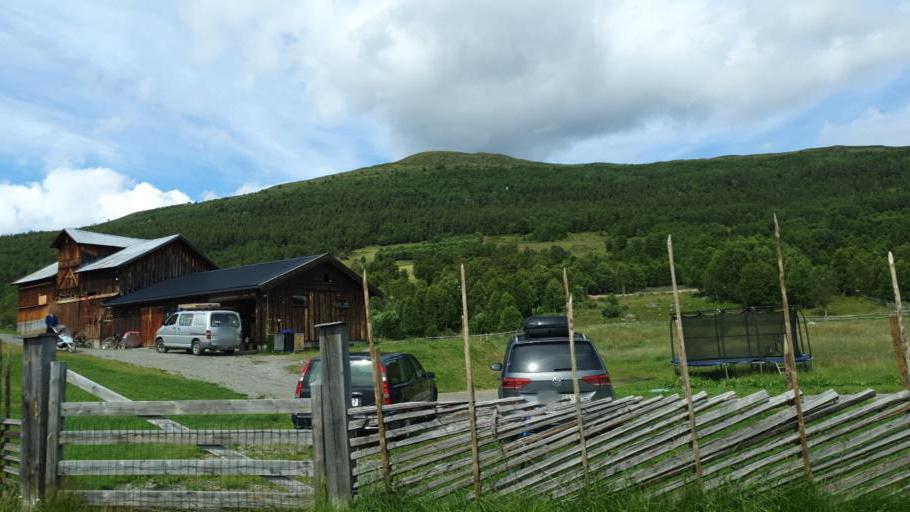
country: NO
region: Oppland
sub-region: Vaga
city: Vagamo
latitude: 61.7288
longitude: 9.0746
